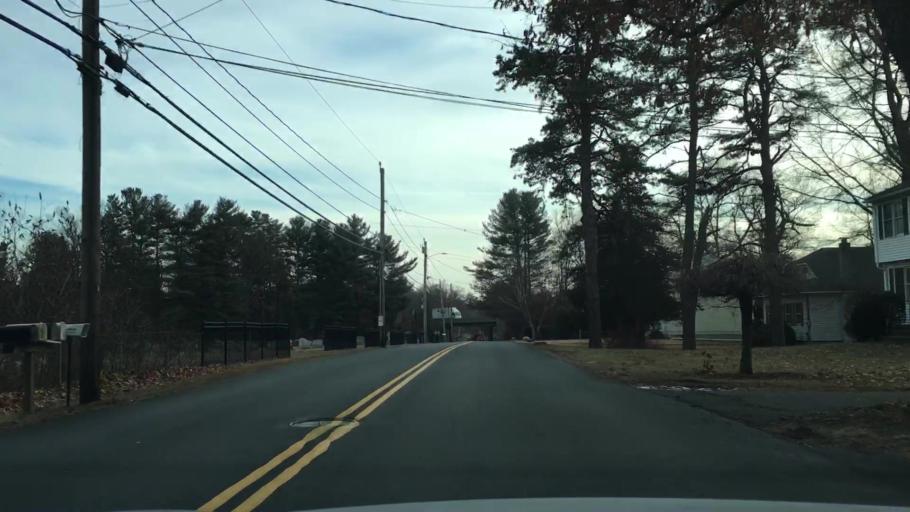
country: US
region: Massachusetts
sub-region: Hampden County
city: Westfield
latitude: 42.1480
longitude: -72.7409
